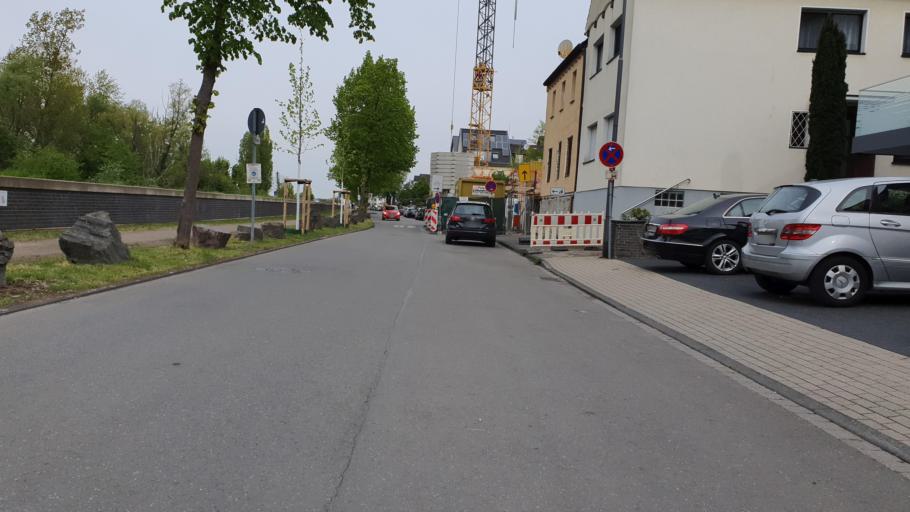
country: DE
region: North Rhine-Westphalia
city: Monheim am Rhein
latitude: 51.0593
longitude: 6.9181
